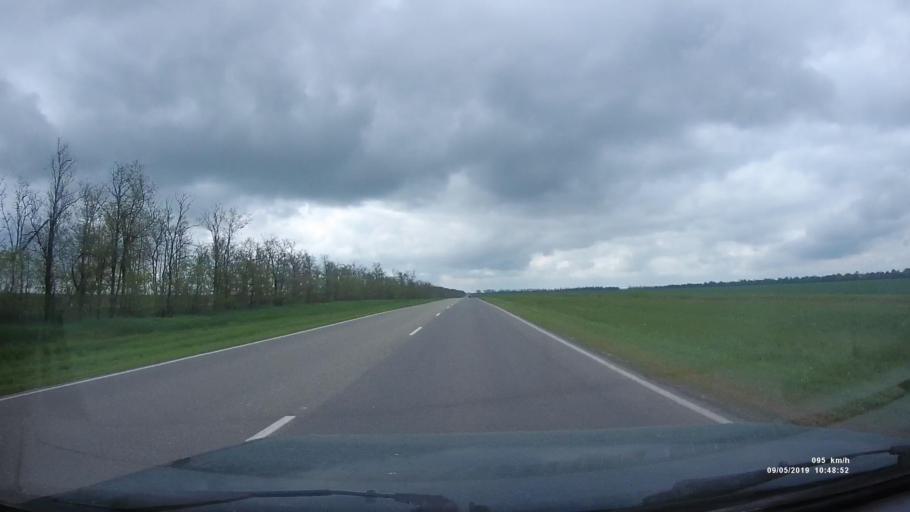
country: RU
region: Rostov
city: Peshkovo
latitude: 46.9504
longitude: 39.3557
